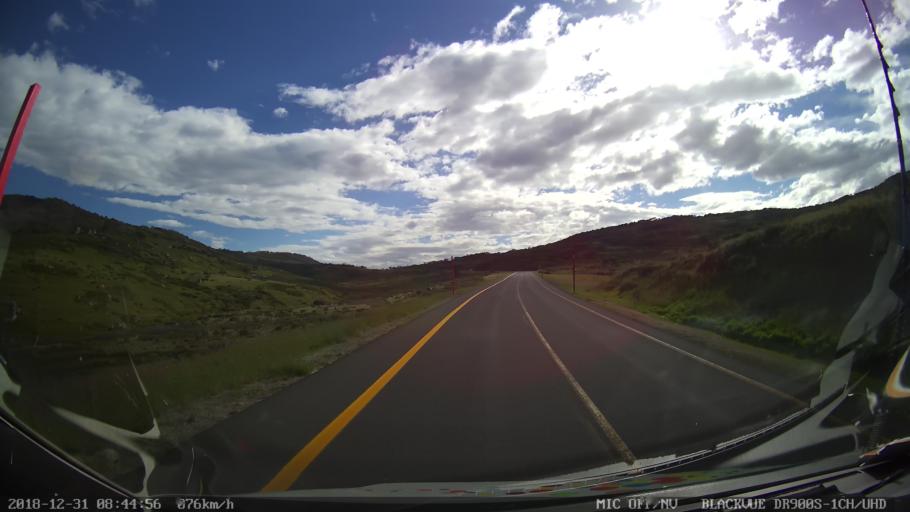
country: AU
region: New South Wales
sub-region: Snowy River
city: Jindabyne
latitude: -36.3797
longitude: 148.4595
